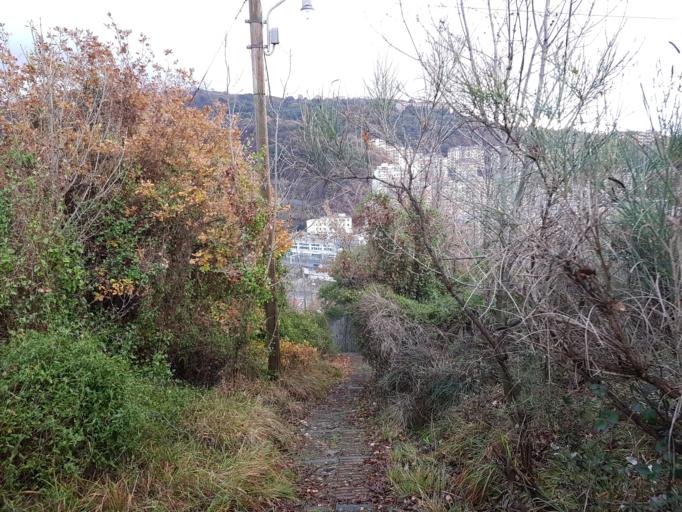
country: IT
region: Liguria
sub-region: Provincia di Genova
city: Genoa
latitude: 44.4284
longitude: 8.9461
